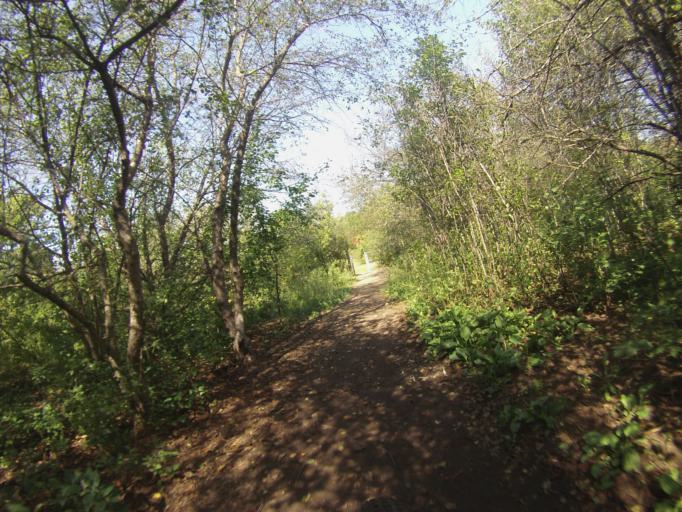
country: CA
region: Ontario
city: Ottawa
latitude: 45.3550
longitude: -75.6243
